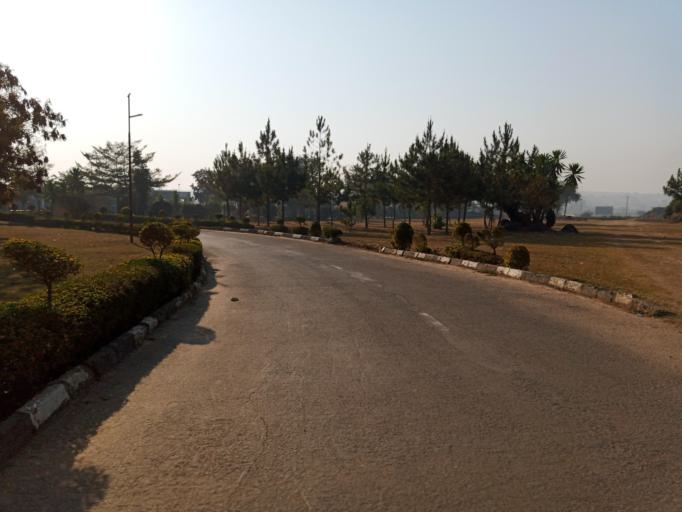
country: ZM
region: Copperbelt
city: Kitwe
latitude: -12.8754
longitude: 28.2528
